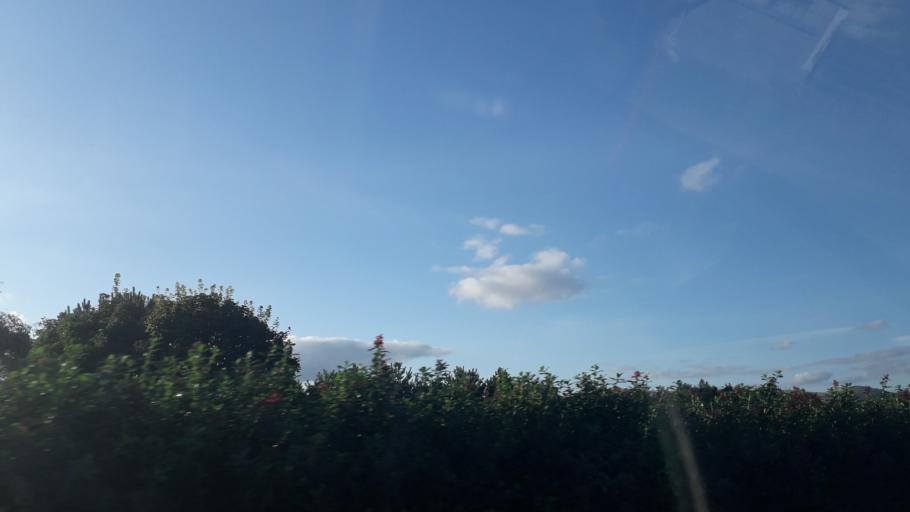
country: IE
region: Leinster
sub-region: Lu
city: Carlingford
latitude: 54.0242
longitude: -6.1391
